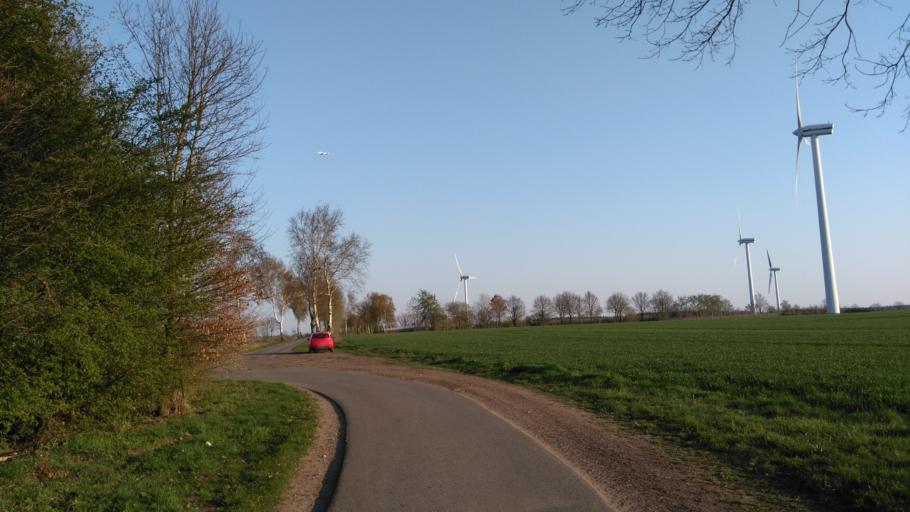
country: DE
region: Lower Saxony
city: Nottensdorf
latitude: 53.4581
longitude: 9.5937
